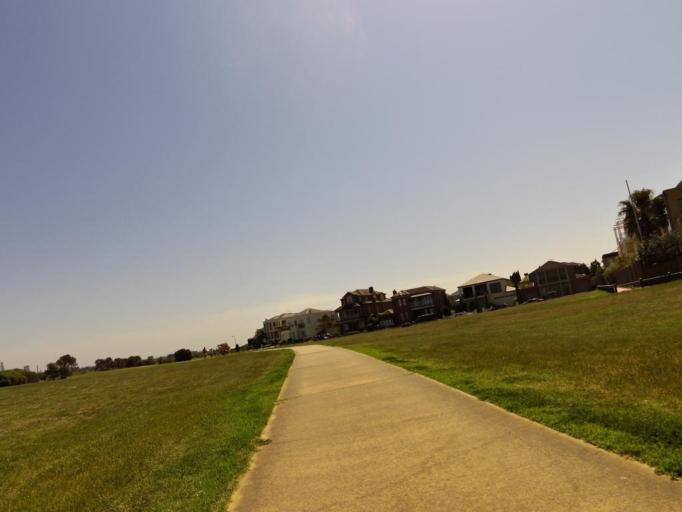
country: AU
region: Victoria
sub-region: Hobsons Bay
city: Williamstown North
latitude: -37.8639
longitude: 144.8777
